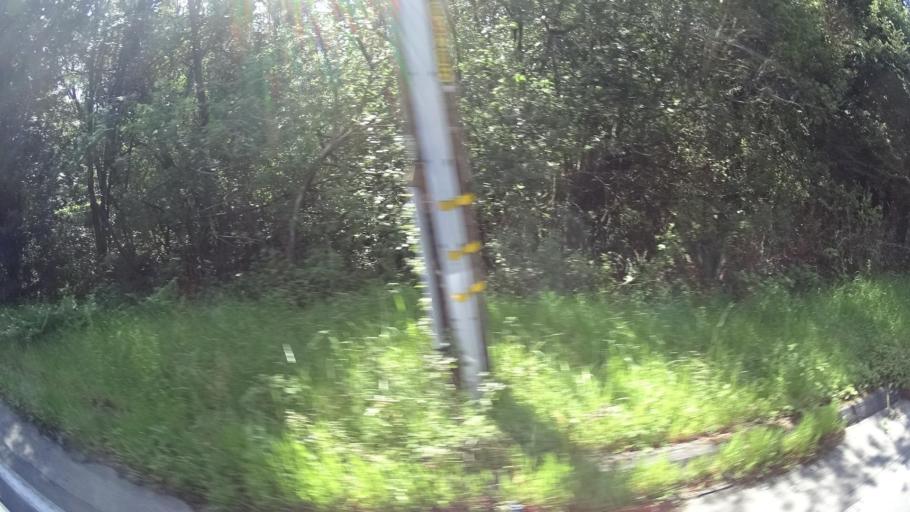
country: US
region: California
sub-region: Humboldt County
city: Hydesville
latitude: 40.5550
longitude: -124.1045
